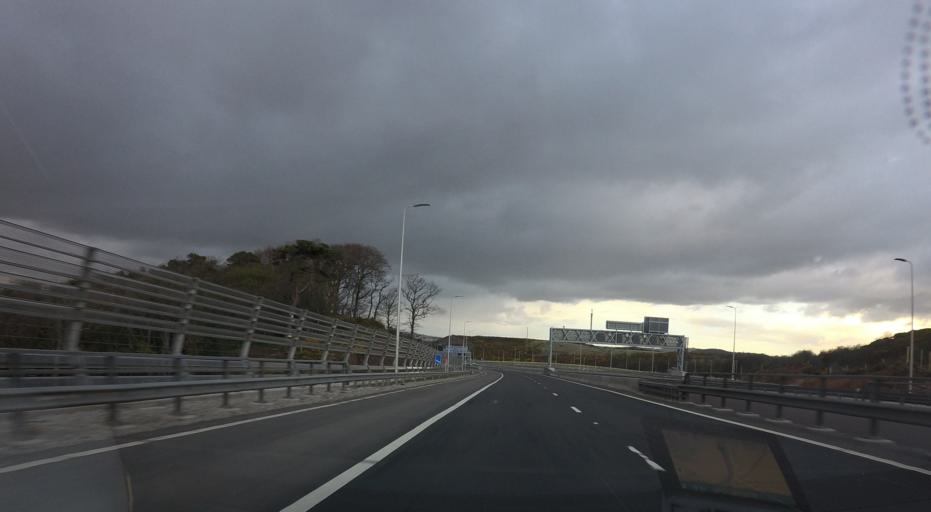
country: GB
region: Scotland
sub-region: Fife
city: North Queensferry
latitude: 56.0142
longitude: -3.4069
